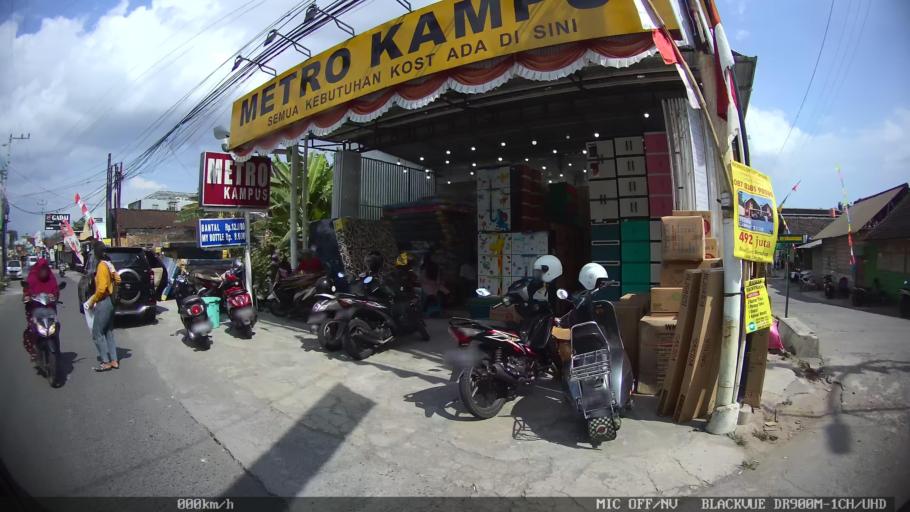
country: ID
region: Daerah Istimewa Yogyakarta
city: Kasihan
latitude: -7.8153
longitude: 110.3259
